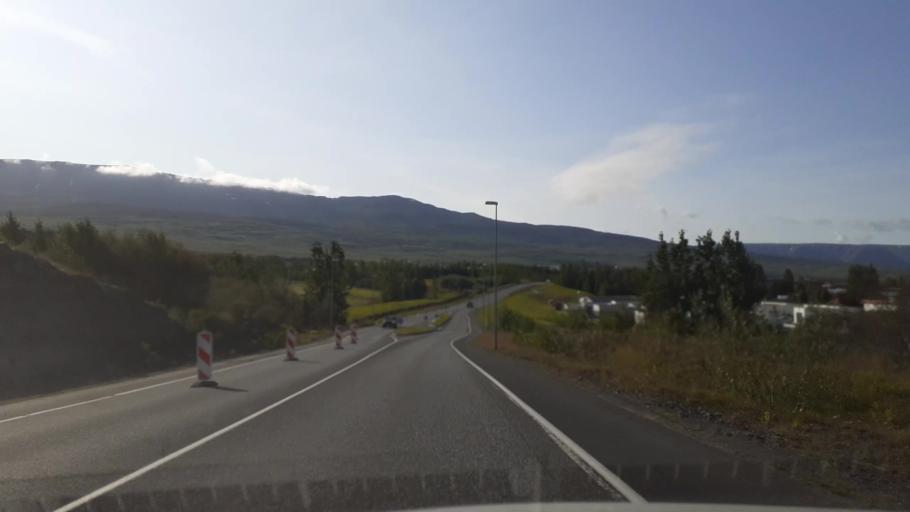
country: IS
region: Northeast
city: Akureyri
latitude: 65.6714
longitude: -18.1166
